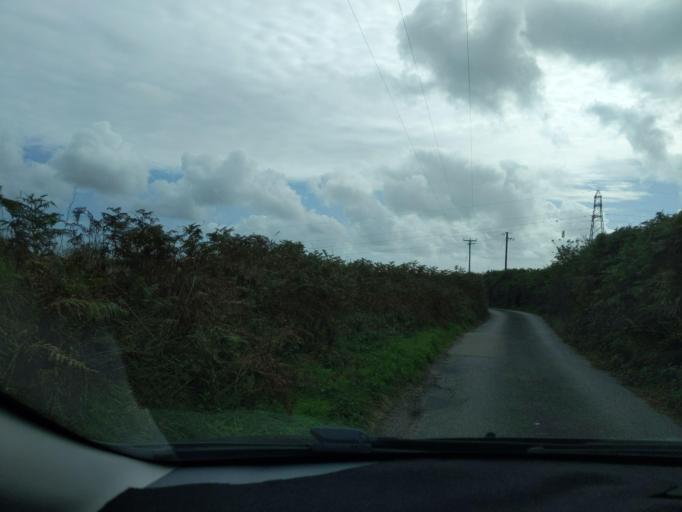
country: GB
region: England
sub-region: Cornwall
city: Par
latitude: 50.3878
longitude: -4.7022
